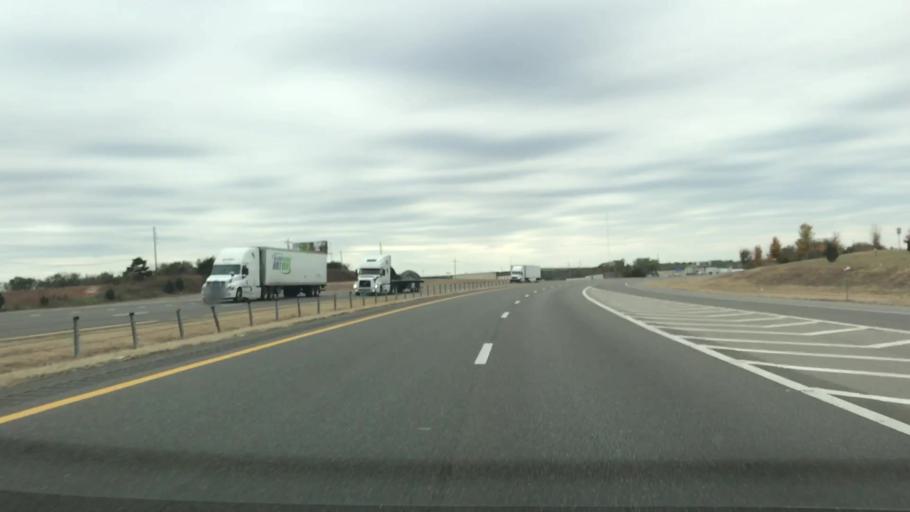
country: US
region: Oklahoma
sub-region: Custer County
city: Weatherford
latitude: 35.5222
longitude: -98.6959
